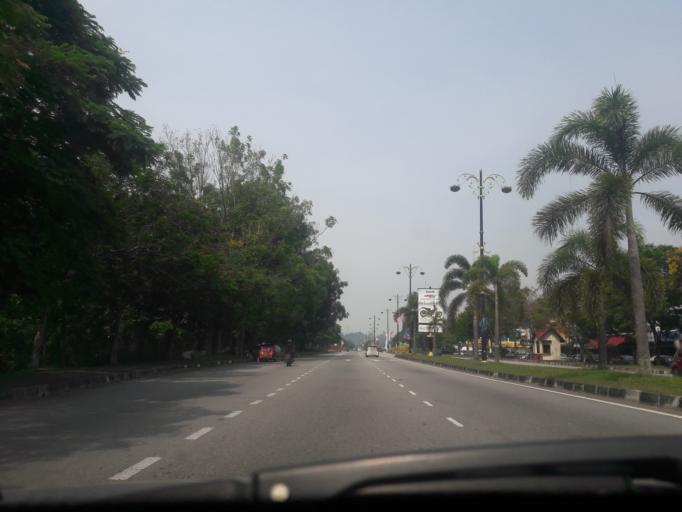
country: MY
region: Kedah
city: Kulim
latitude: 5.3886
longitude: 100.5623
